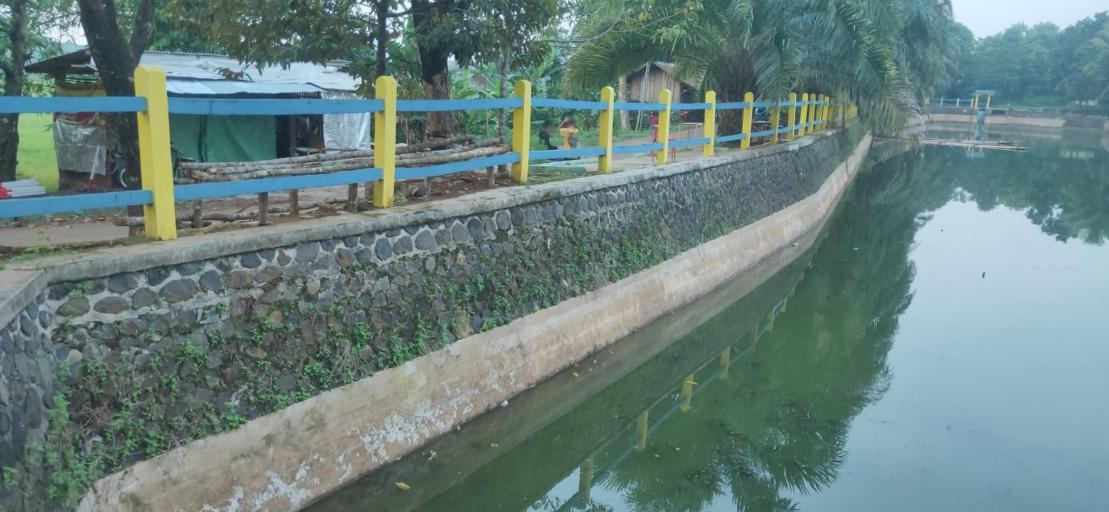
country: ID
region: West Java
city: Pangradin Satu
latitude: -6.4699
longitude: 106.4437
